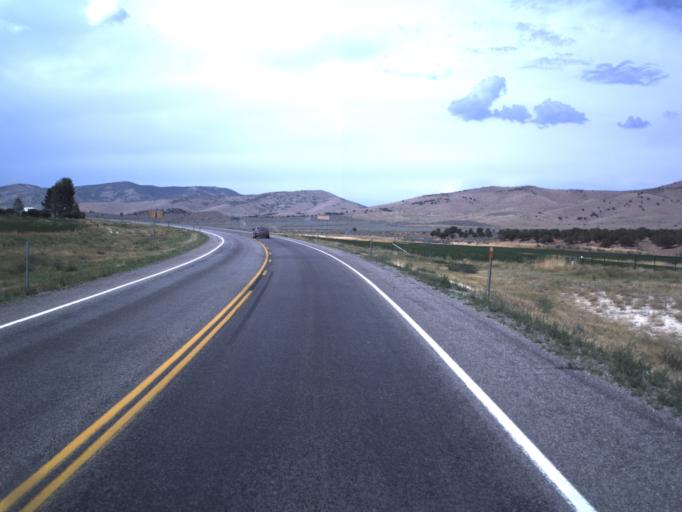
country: US
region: Utah
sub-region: Sanpete County
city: Fountain Green
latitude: 39.6382
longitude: -111.6344
